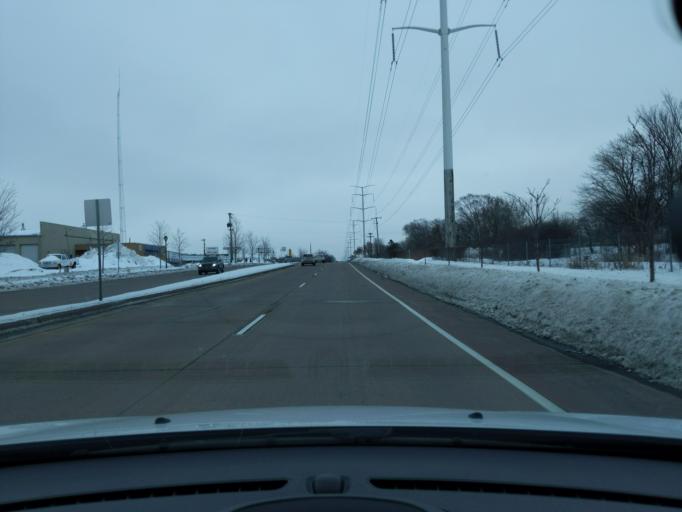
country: US
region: Minnesota
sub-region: Ramsey County
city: Roseville
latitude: 45.0213
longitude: -93.1757
